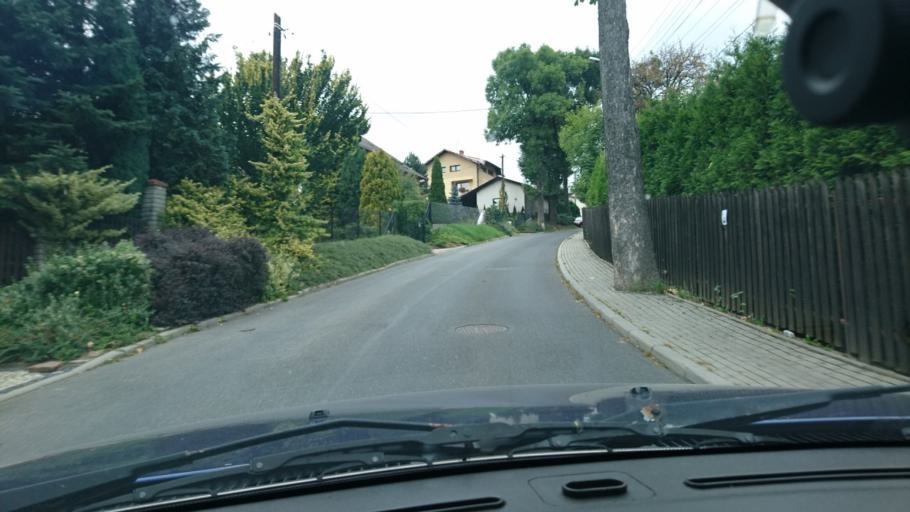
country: PL
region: Silesian Voivodeship
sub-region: Bielsko-Biala
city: Bielsko-Biala
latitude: 49.8257
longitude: 19.0114
